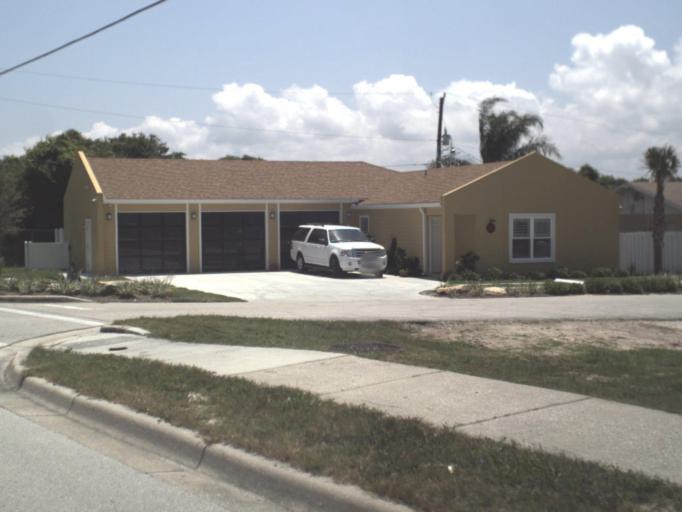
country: US
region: Florida
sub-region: Saint Johns County
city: Butler Beach
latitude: 29.8089
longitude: -81.2667
